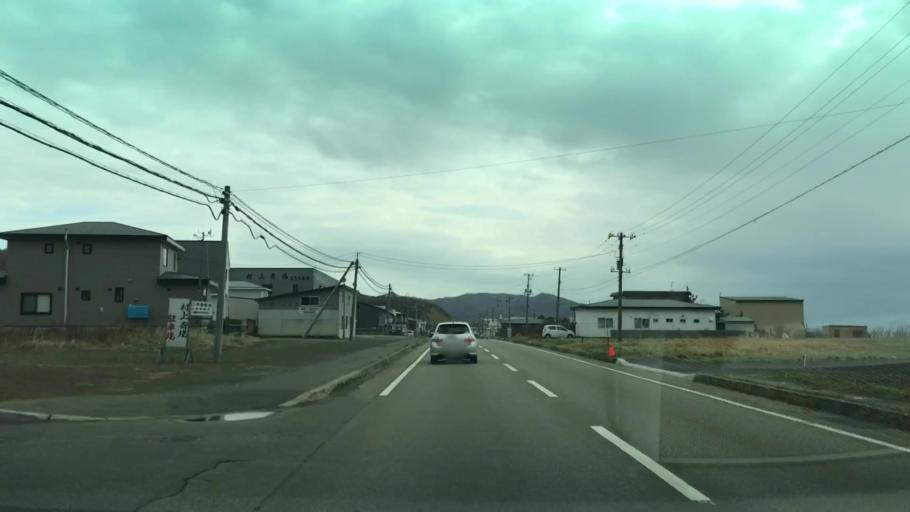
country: JP
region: Hokkaido
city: Shizunai-furukawacho
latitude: 42.0267
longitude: 143.1375
